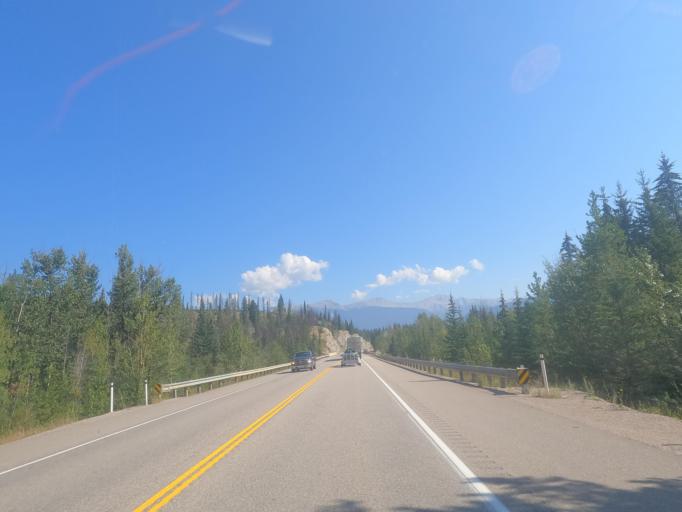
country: CA
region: Alberta
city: Jasper Park Lodge
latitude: 52.8627
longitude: -118.1079
